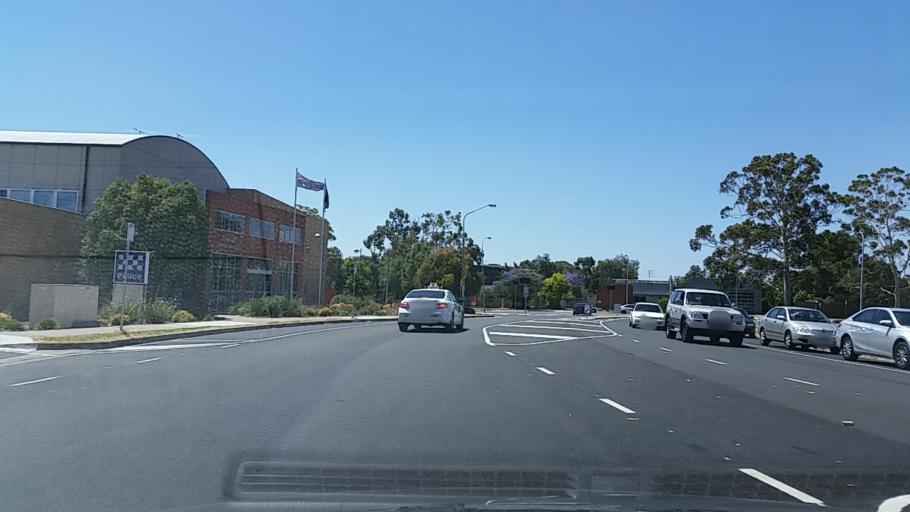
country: AU
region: South Australia
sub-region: Salisbury
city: Elizabeth
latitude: -34.7160
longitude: 138.6714
